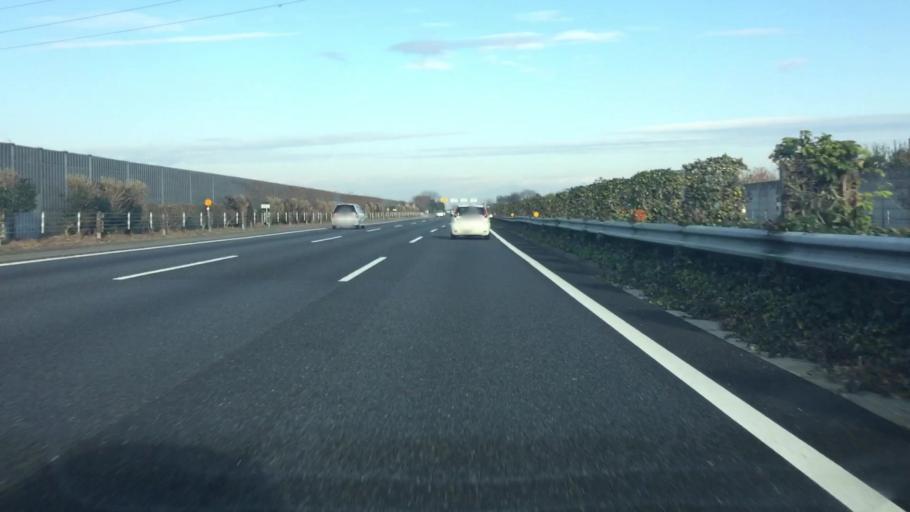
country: JP
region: Saitama
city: Honjo
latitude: 36.2374
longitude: 139.1468
